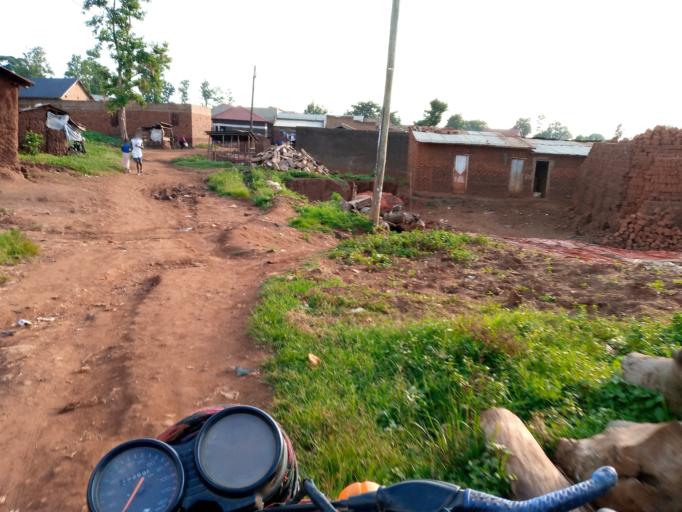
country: UG
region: Eastern Region
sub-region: Mbale District
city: Mbale
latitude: 1.0828
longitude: 34.1569
